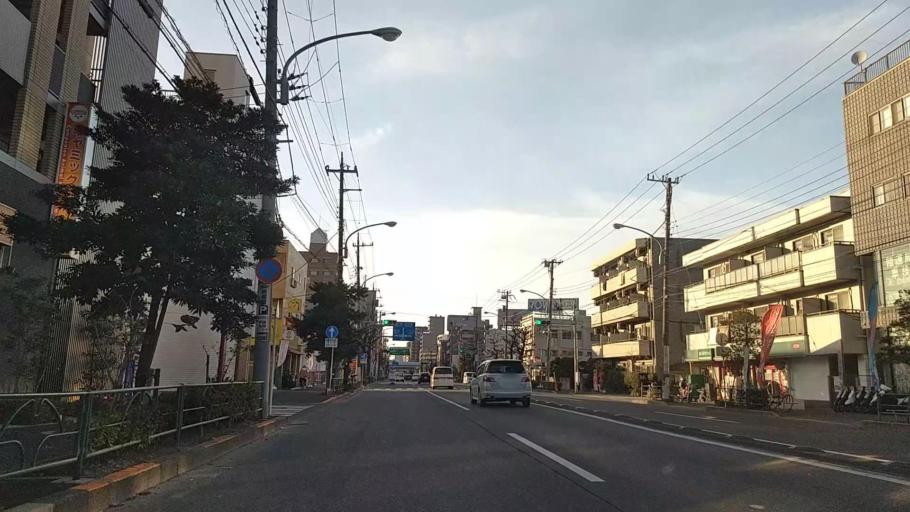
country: JP
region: Tokyo
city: Urayasu
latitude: 35.6668
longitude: 139.8780
